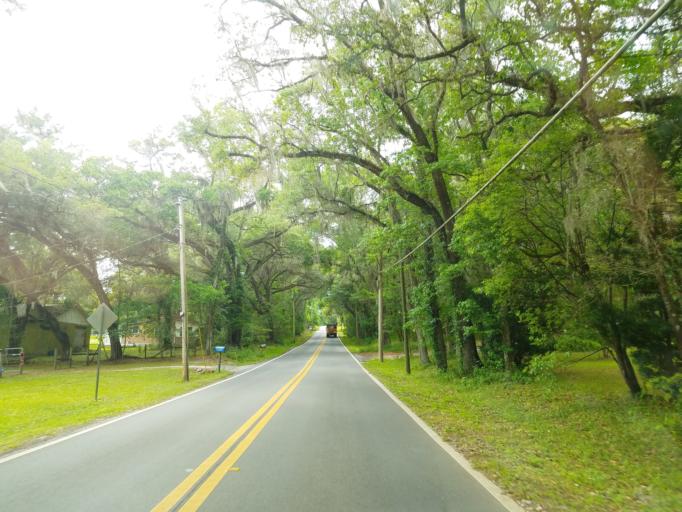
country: US
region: Florida
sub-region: Hernando County
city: Brooksville
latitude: 28.5562
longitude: -82.3684
